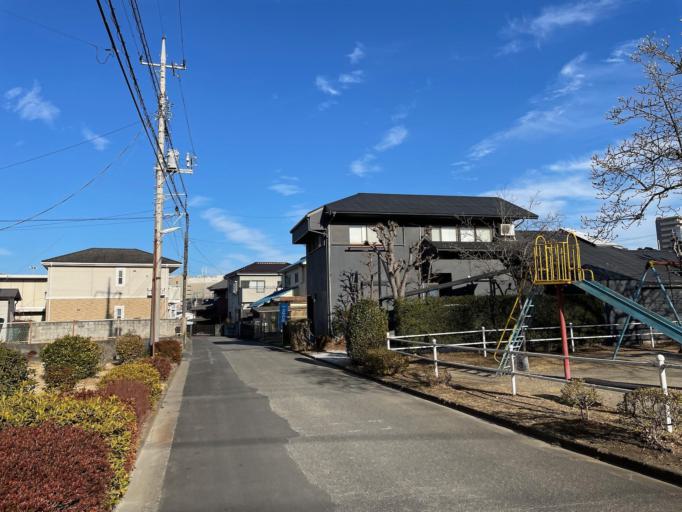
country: JP
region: Saitama
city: Sayama
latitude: 35.8353
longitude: 139.3828
